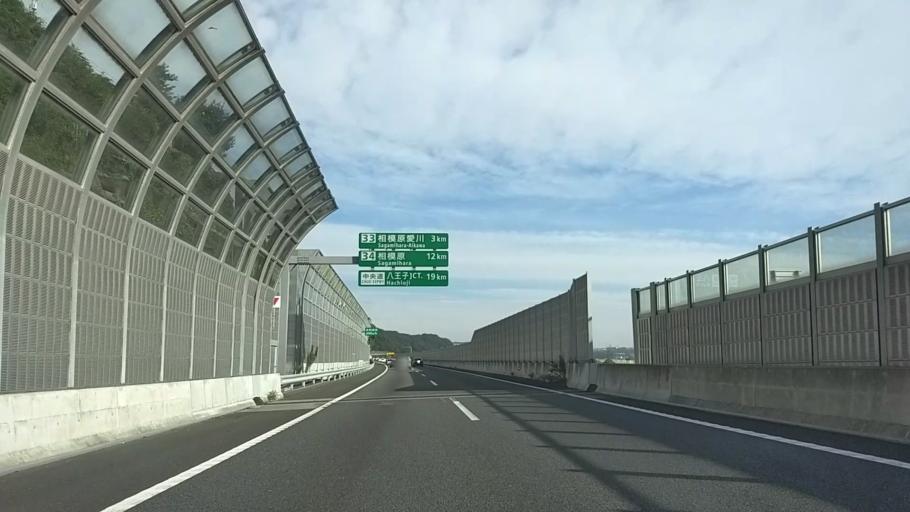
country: JP
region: Kanagawa
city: Zama
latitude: 35.4945
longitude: 139.3676
